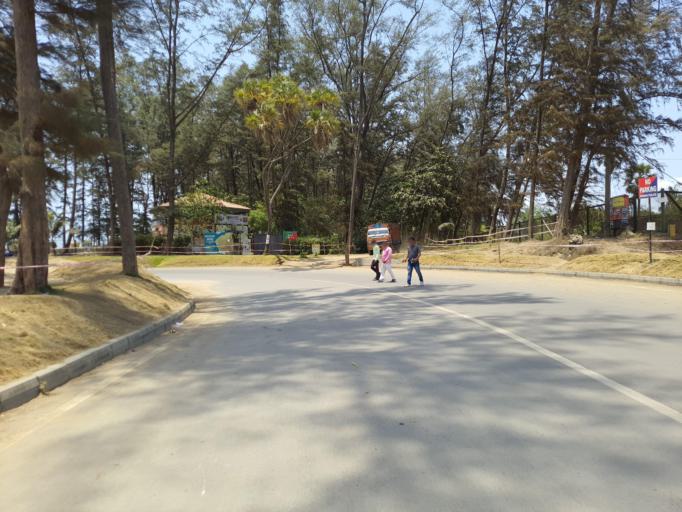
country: IN
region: Daman and Diu
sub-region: Daman District
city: Daman
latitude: 20.3786
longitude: 72.8248
